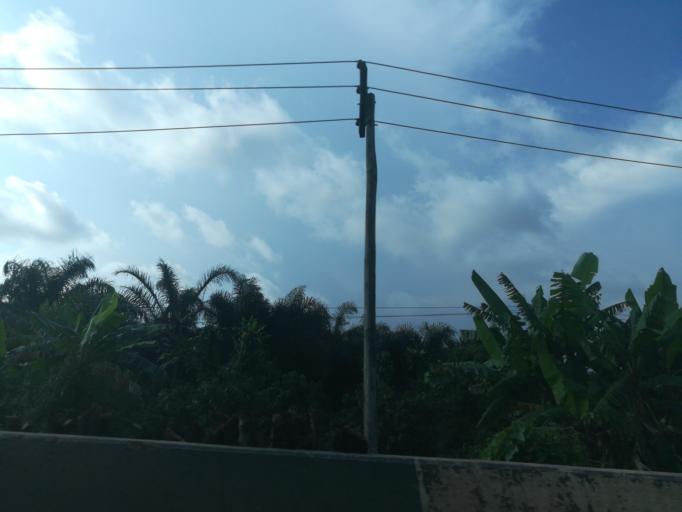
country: NG
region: Ogun
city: Ado Odo
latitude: 6.4922
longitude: 3.0792
